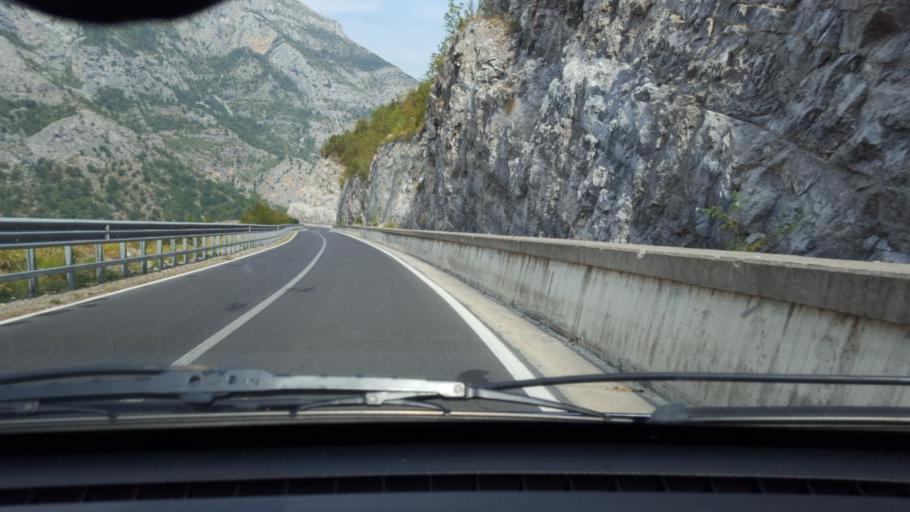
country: AL
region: Shkoder
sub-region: Rrethi i Malesia e Madhe
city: Kastrat
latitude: 42.4188
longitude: 19.5024
